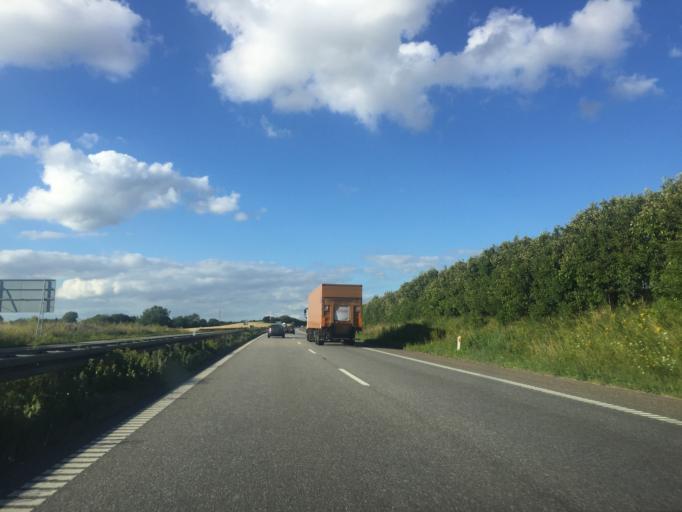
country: DK
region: Zealand
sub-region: Faxe Kommune
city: Ronnede
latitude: 55.1772
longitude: 11.9600
